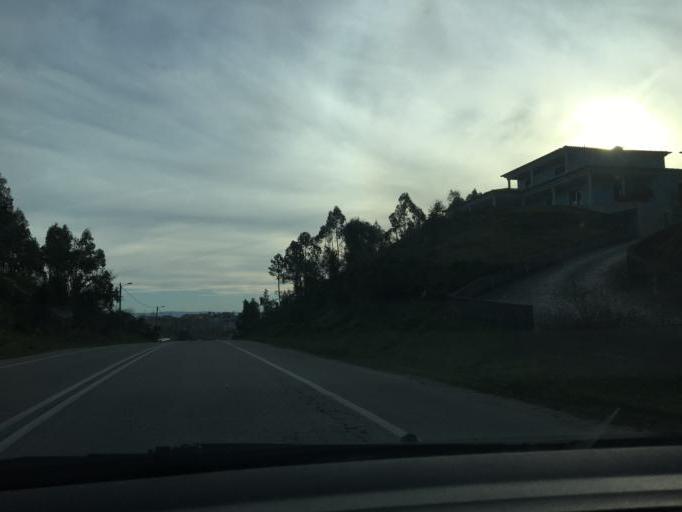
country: PT
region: Coimbra
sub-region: Montemor-O-Velho
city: Arazede
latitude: 40.2184
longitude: -8.5939
